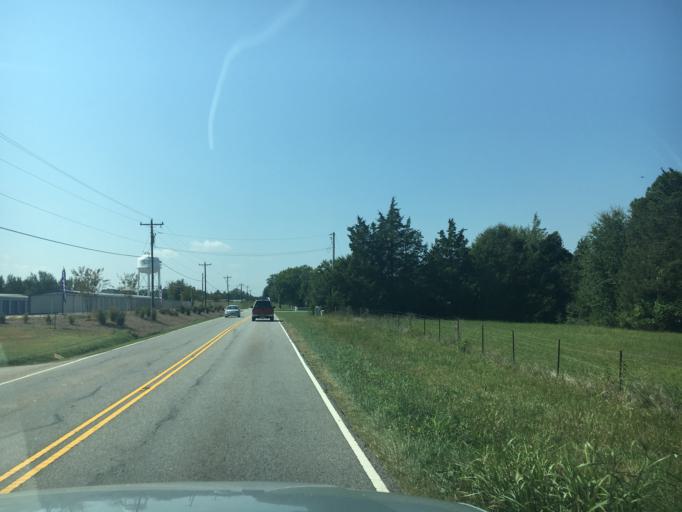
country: US
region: South Carolina
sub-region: Anderson County
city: Centerville
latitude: 34.5149
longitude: -82.7445
